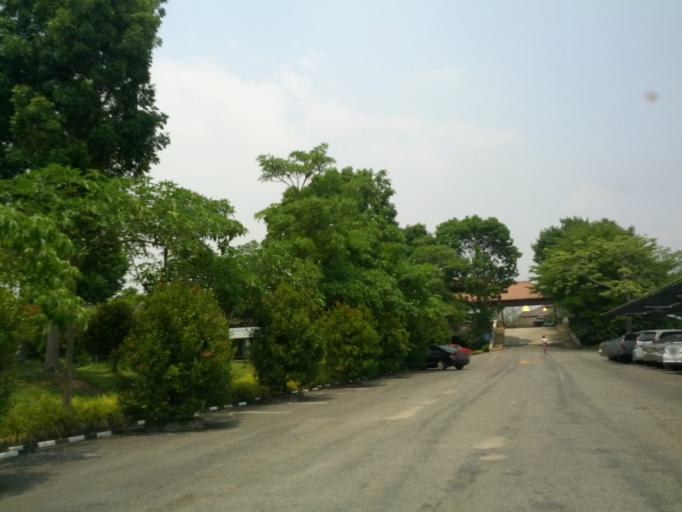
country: TH
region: Chiang Mai
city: San Sai
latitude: 18.9114
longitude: 99.0381
